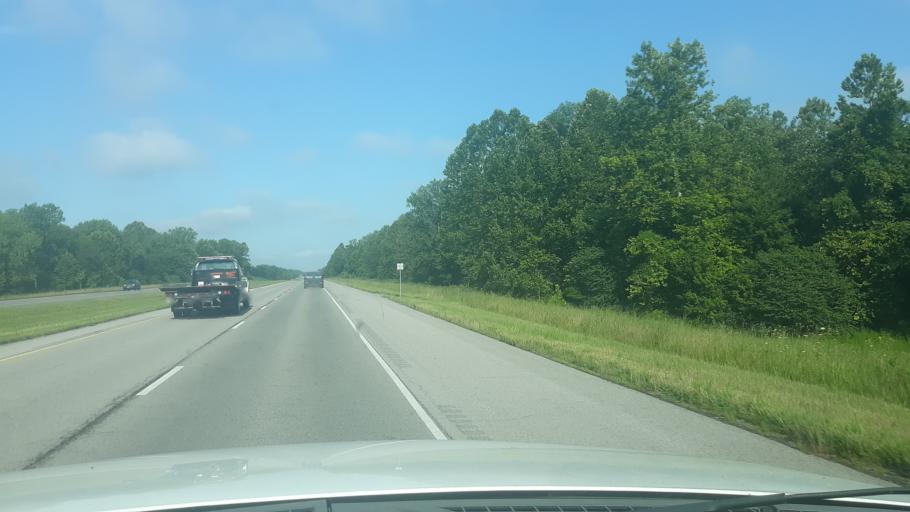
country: US
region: Illinois
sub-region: Saline County
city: Carrier Mills
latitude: 37.7309
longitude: -88.7372
